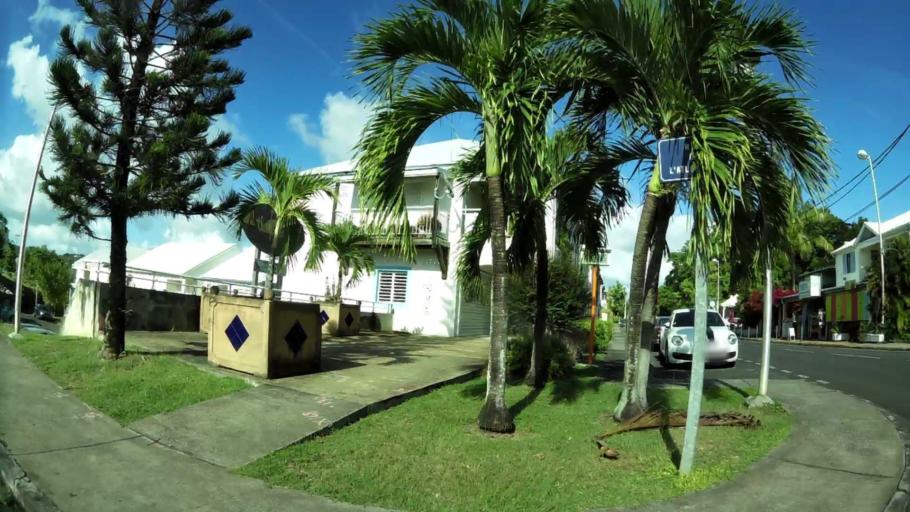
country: GP
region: Guadeloupe
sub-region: Guadeloupe
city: Le Gosier
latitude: 16.2073
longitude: -61.5013
